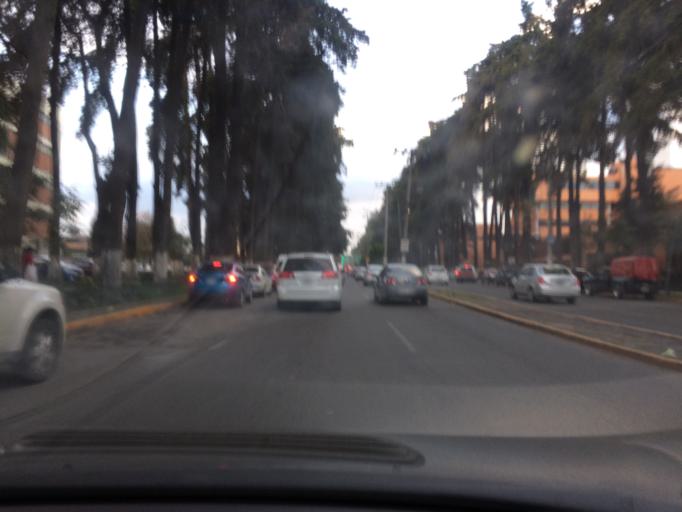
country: MX
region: Mexico
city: San Buenaventura
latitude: 19.2727
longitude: -99.6600
